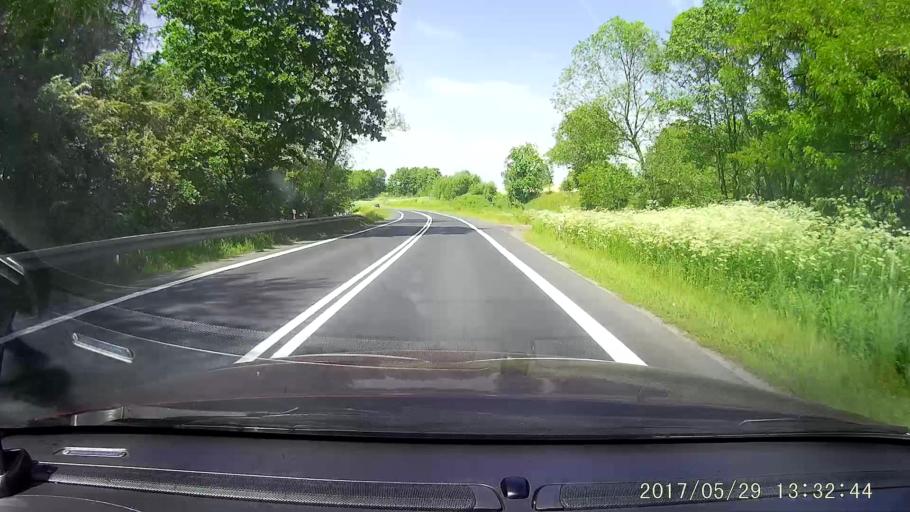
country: PL
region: Lower Silesian Voivodeship
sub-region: Powiat lubanski
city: Luban
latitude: 51.0888
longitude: 15.3224
